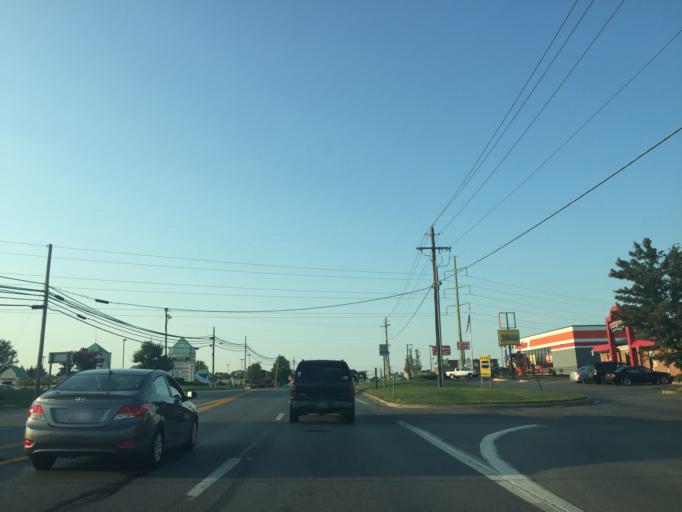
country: US
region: Maryland
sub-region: Frederick County
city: Frederick
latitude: 39.3912
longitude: -77.4093
